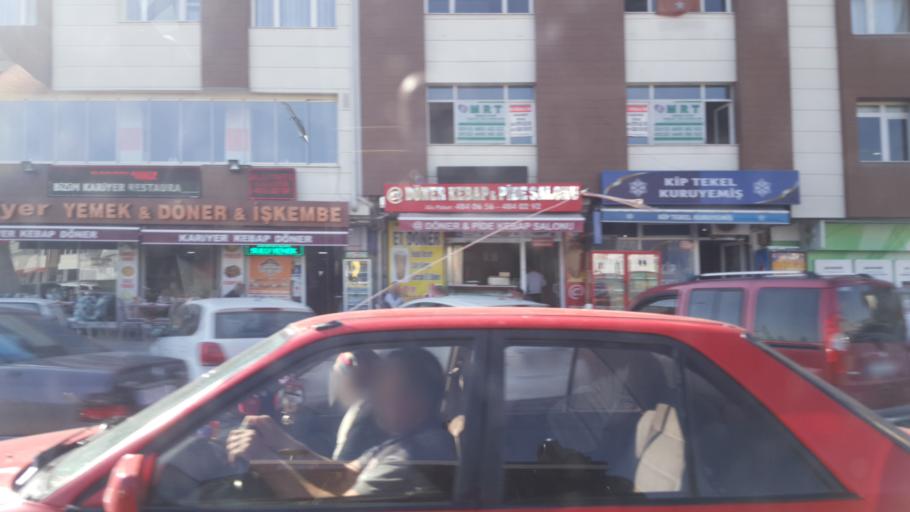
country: TR
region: Ankara
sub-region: Goelbasi
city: Golbasi
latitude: 39.7935
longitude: 32.8065
